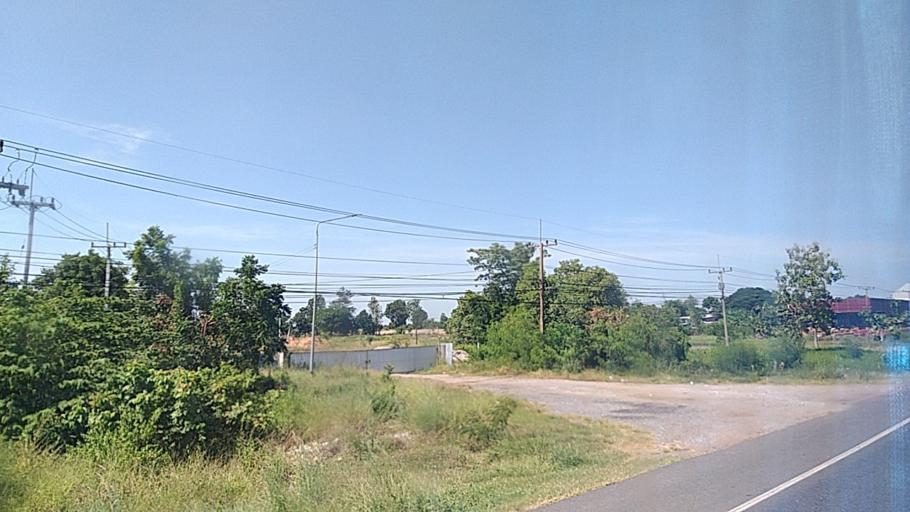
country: TH
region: Khon Kaen
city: Ban Haet
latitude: 16.2900
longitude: 102.7863
